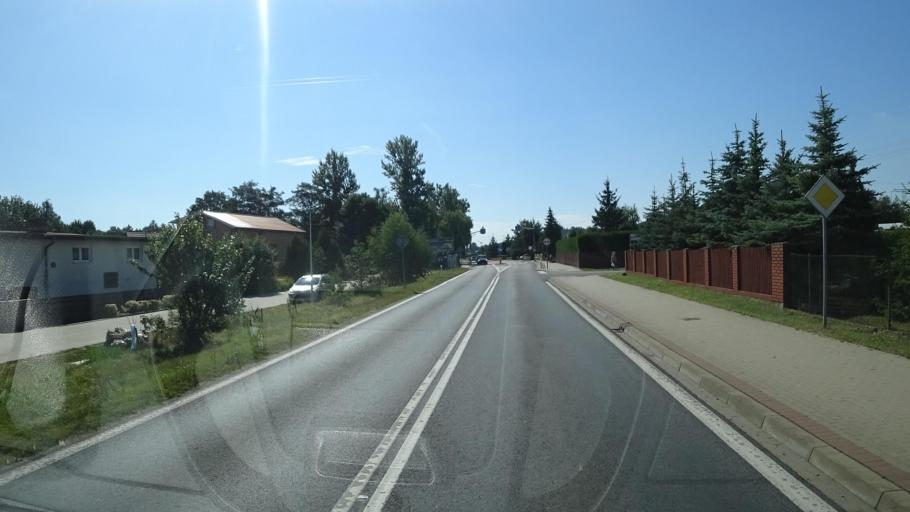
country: PL
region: Greater Poland Voivodeship
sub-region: Powiat koninski
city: Slesin
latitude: 52.3463
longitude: 18.2987
